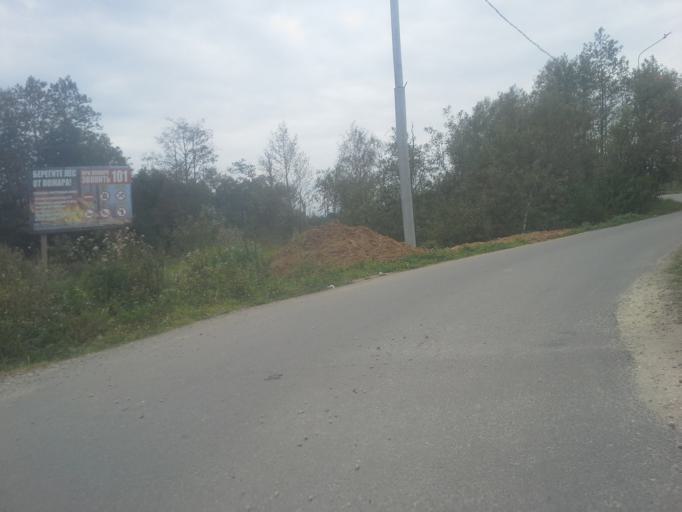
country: RU
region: Moskovskaya
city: Kievskij
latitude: 55.4260
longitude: 36.8920
